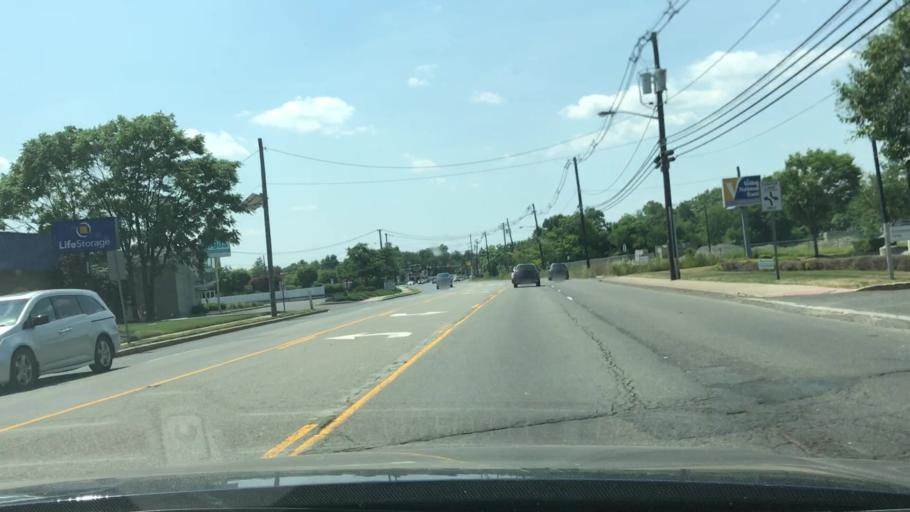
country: US
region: New Jersey
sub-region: Middlesex County
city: Society Hill
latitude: 40.5603
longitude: -74.4442
